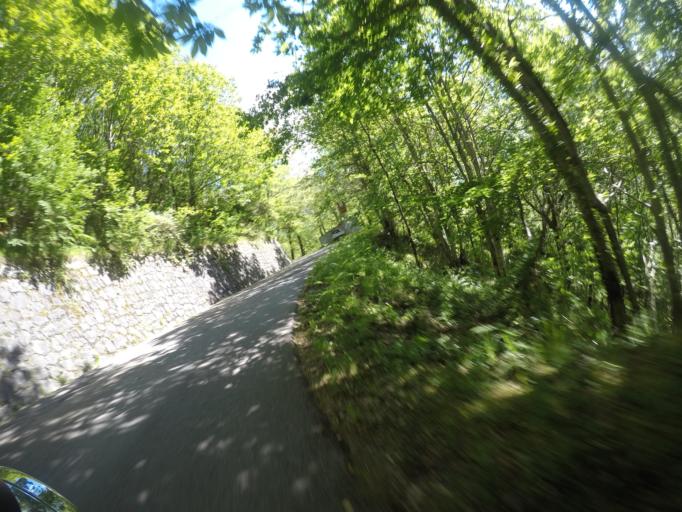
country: IT
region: Tuscany
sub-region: Provincia di Lucca
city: Fontana delle Monache
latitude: 44.0640
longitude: 10.3086
